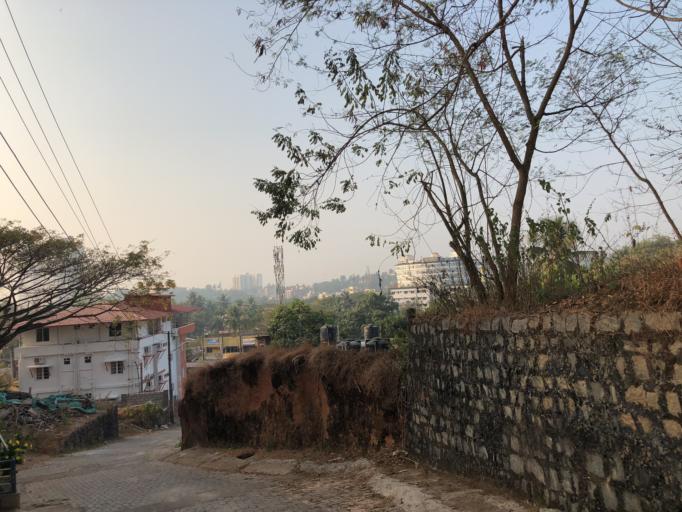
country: IN
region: Karnataka
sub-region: Dakshina Kannada
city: Mangalore
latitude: 12.8701
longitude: 74.8675
